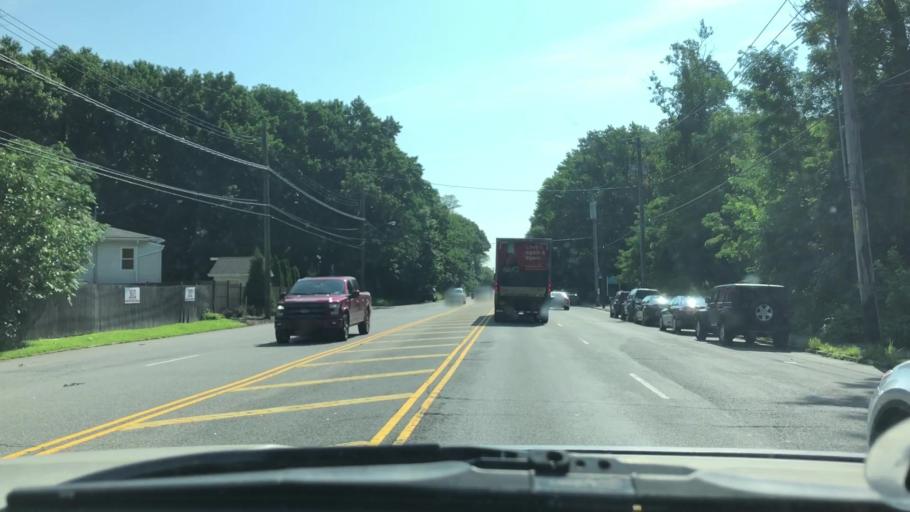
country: US
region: New York
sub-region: Richmond County
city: Staten Island
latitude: 40.5267
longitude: -74.1736
